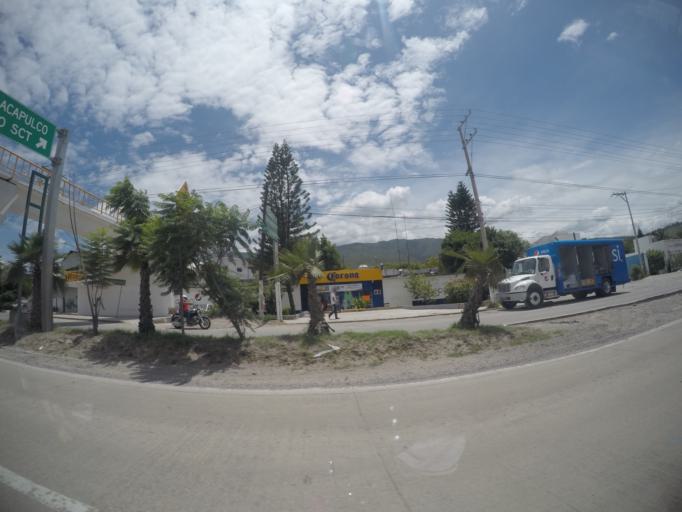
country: MX
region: Guerrero
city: Chilpancingo de los Bravos
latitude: 17.5382
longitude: -99.4999
